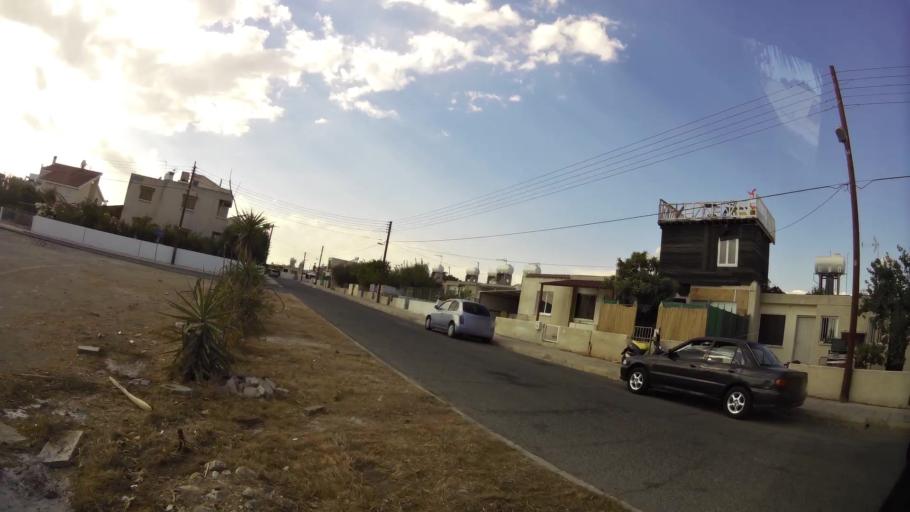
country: CY
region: Larnaka
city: Livadia
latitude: 34.9388
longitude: 33.6137
